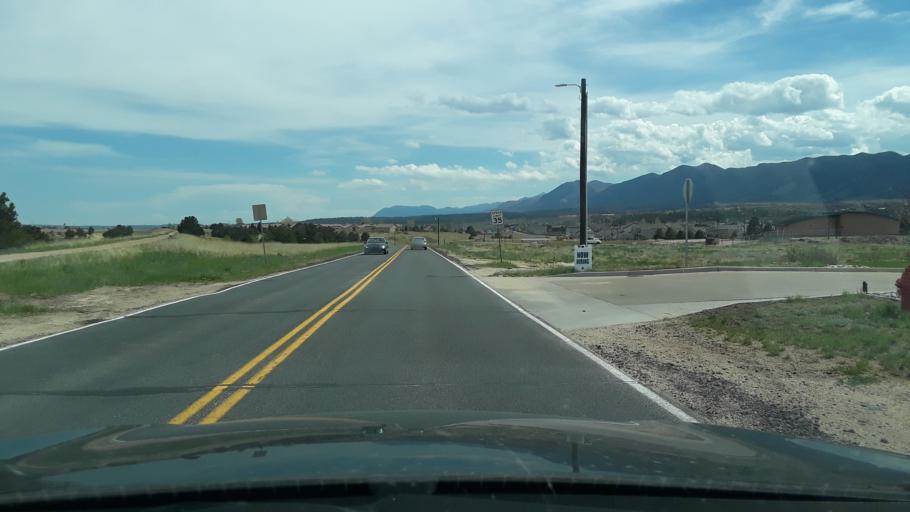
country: US
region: Colorado
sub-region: El Paso County
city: Monument
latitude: 39.0889
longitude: -104.8683
